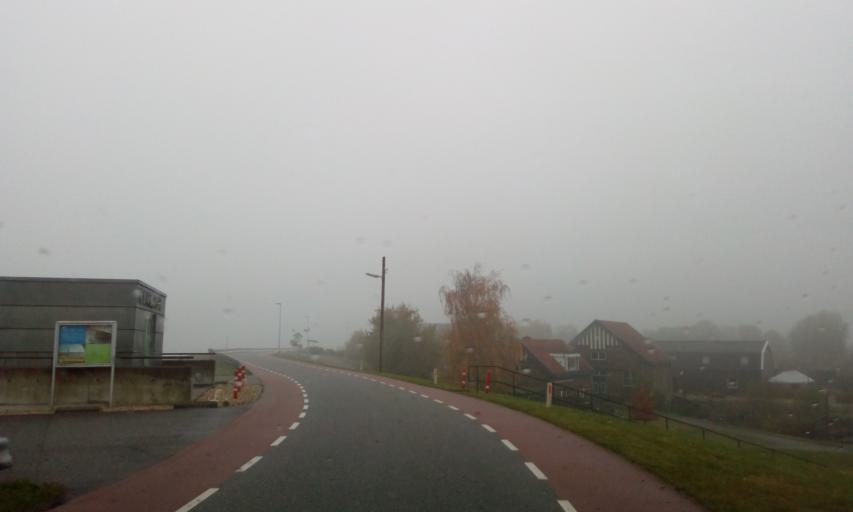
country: NL
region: South Holland
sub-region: Molenwaard
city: Nieuw-Lekkerland
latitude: 51.9076
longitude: 4.7445
